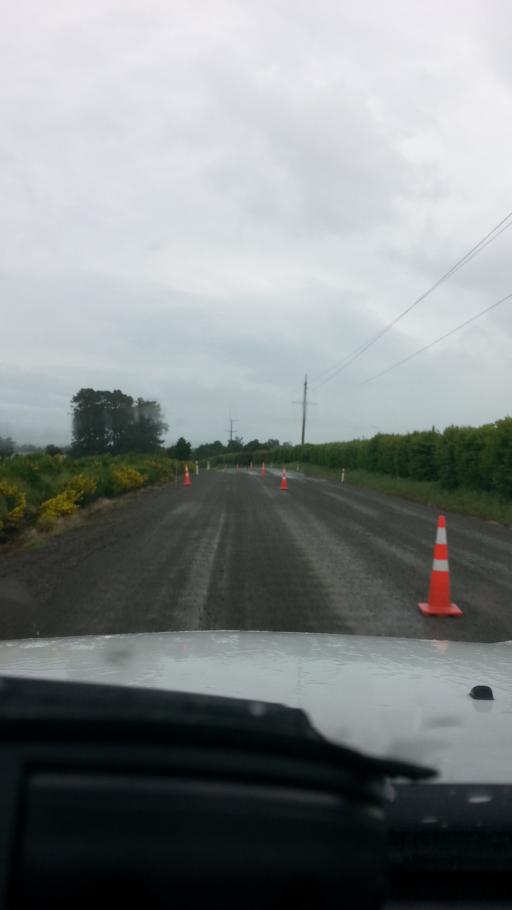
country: NZ
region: Wellington
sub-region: Masterton District
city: Masterton
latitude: -40.8227
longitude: 175.6246
